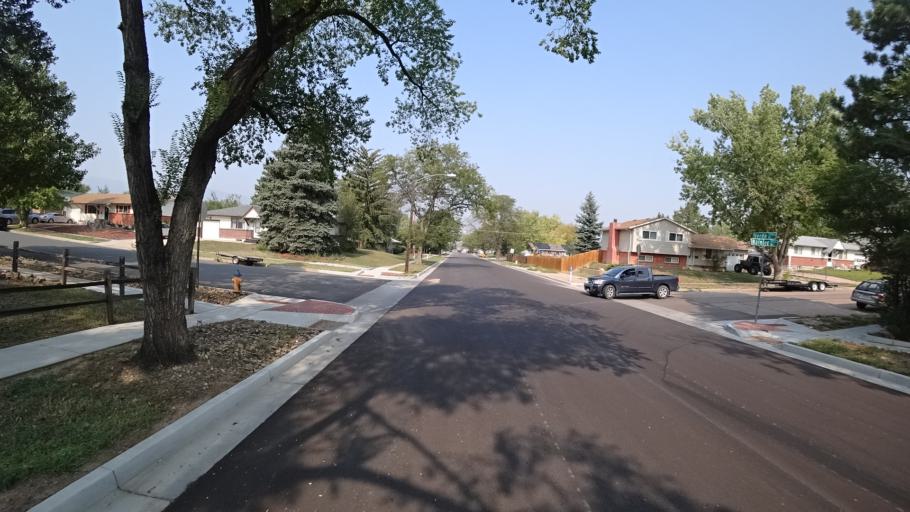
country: US
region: Colorado
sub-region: El Paso County
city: Stratmoor
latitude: 38.8145
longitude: -104.7754
